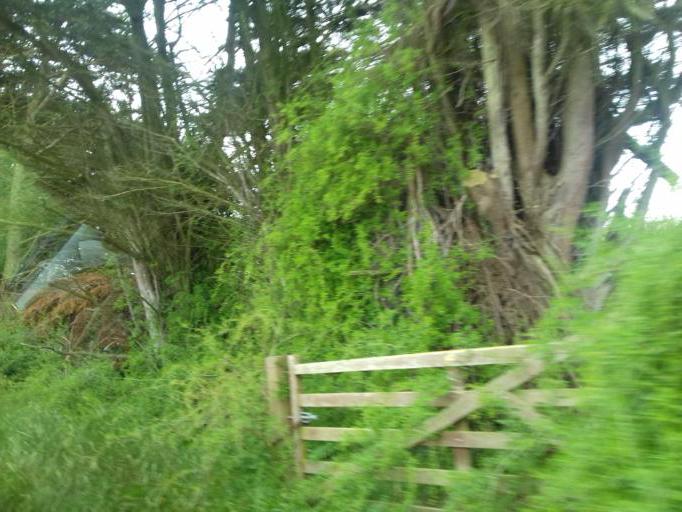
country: IE
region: Leinster
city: Malahide
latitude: 53.4668
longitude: -6.1333
